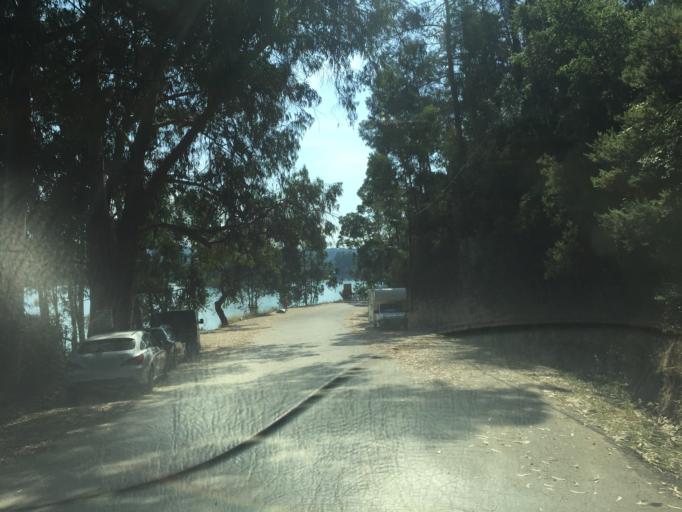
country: PT
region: Santarem
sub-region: Ferreira do Zezere
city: Ferreira do Zezere
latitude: 39.6093
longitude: -8.2806
